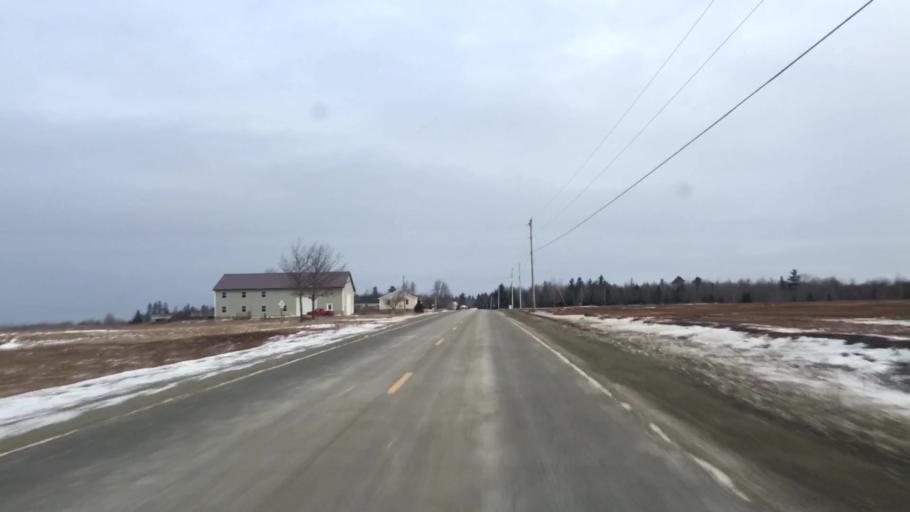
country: US
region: Maine
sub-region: Hancock County
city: Franklin
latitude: 44.7174
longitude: -68.3364
